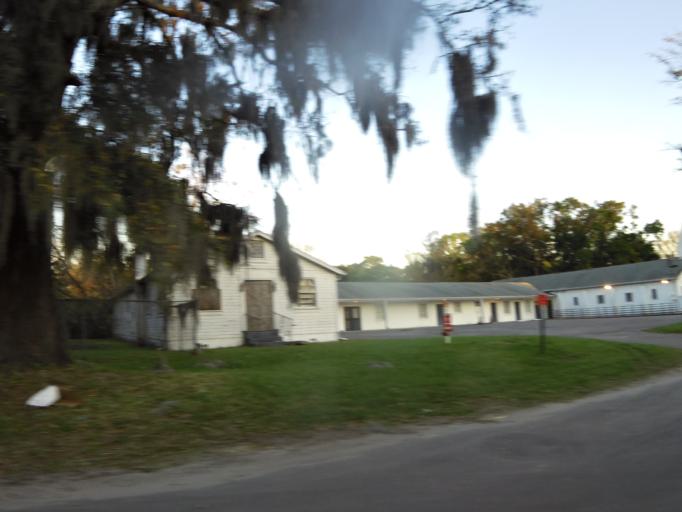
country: US
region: Florida
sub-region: Duval County
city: Jacksonville
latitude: 30.3238
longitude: -81.7013
